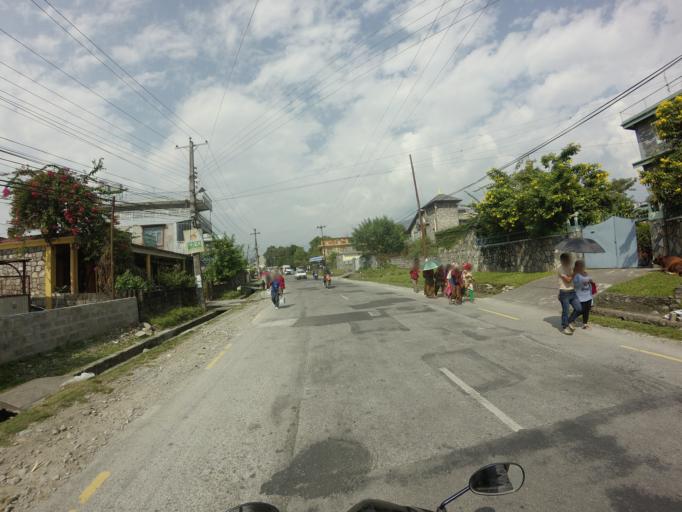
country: NP
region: Western Region
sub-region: Gandaki Zone
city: Pokhara
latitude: 28.2103
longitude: 84.0005
